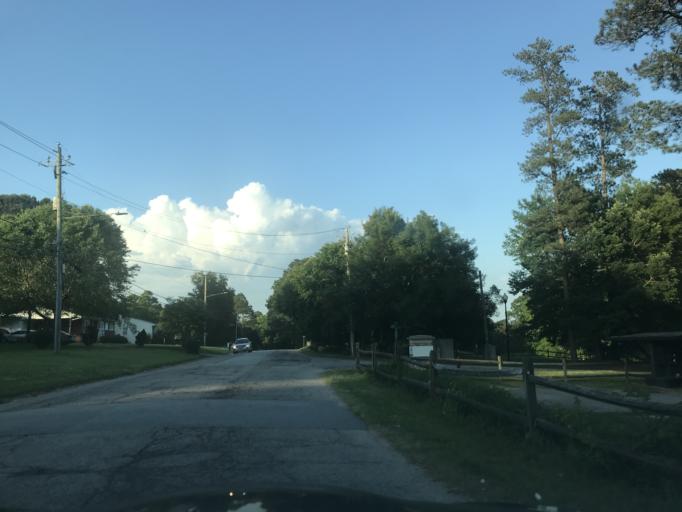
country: US
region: North Carolina
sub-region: Wake County
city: Raleigh
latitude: 35.7425
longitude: -78.6652
